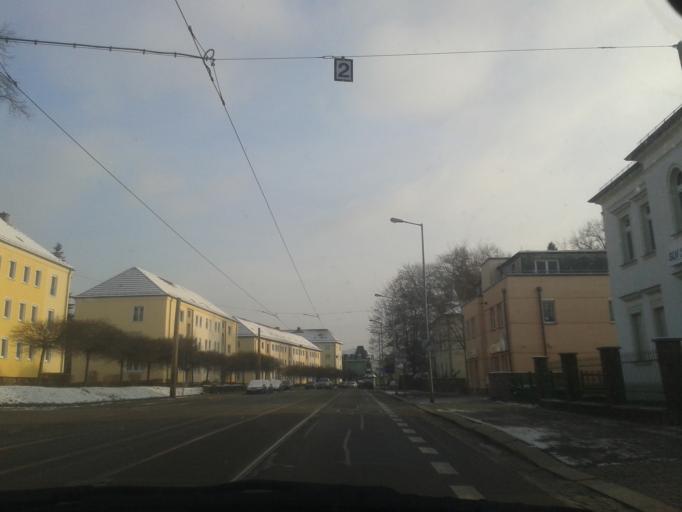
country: DE
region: Saxony
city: Radebeul
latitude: 51.1018
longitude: 13.6825
